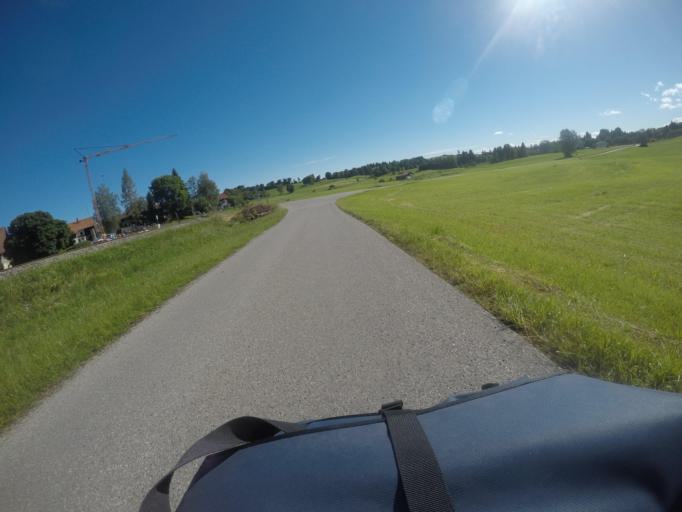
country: DE
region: Bavaria
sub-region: Swabia
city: Oy-Mittelberg
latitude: 47.6280
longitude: 10.4655
